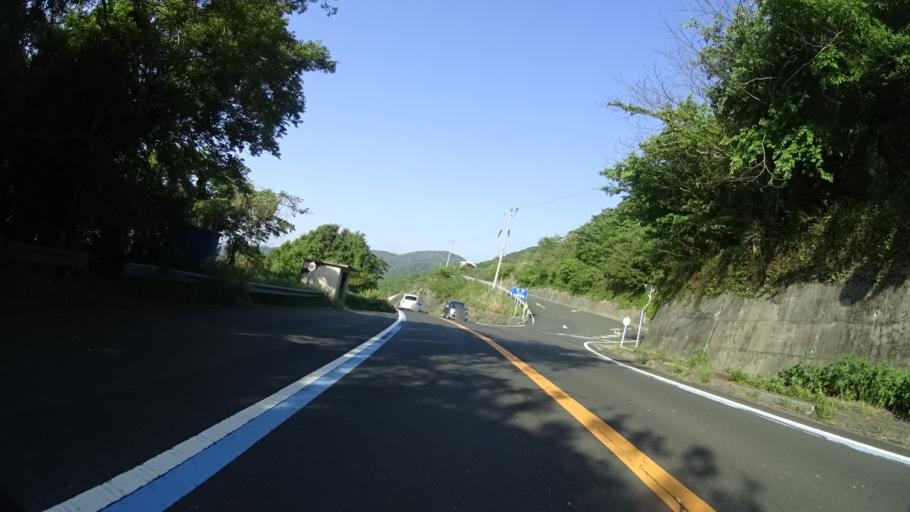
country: JP
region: Ehime
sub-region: Nishiuwa-gun
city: Ikata-cho
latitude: 33.3979
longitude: 132.1617
